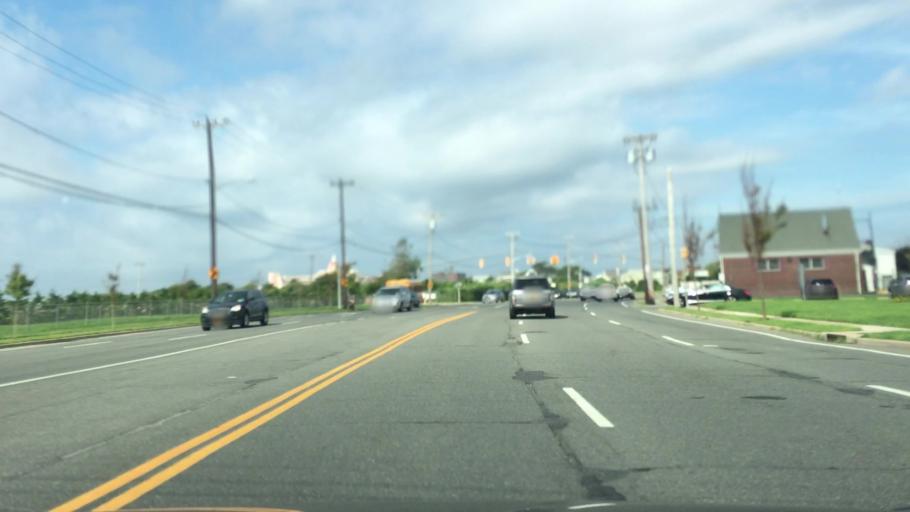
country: US
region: New York
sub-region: Nassau County
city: Lido Beach
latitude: 40.5878
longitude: -73.6286
